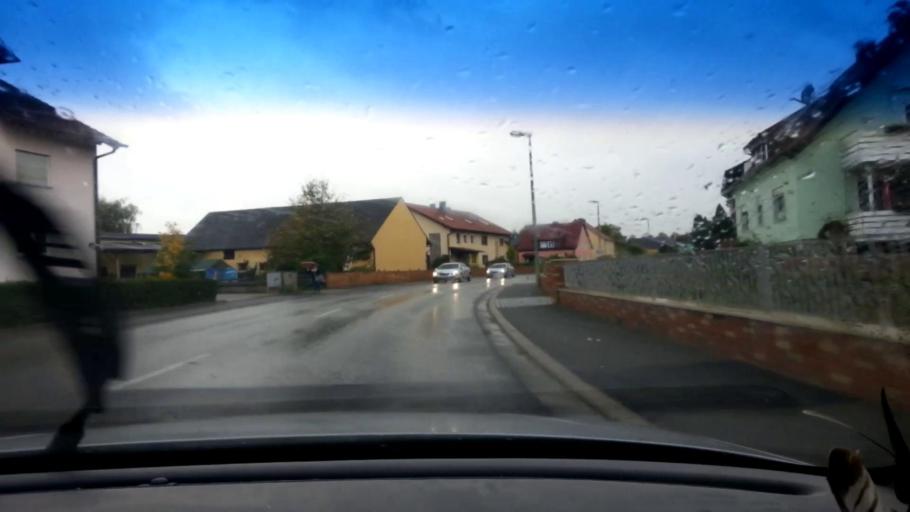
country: DE
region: Bavaria
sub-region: Upper Franconia
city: Walsdorf
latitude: 49.8726
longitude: 10.7980
